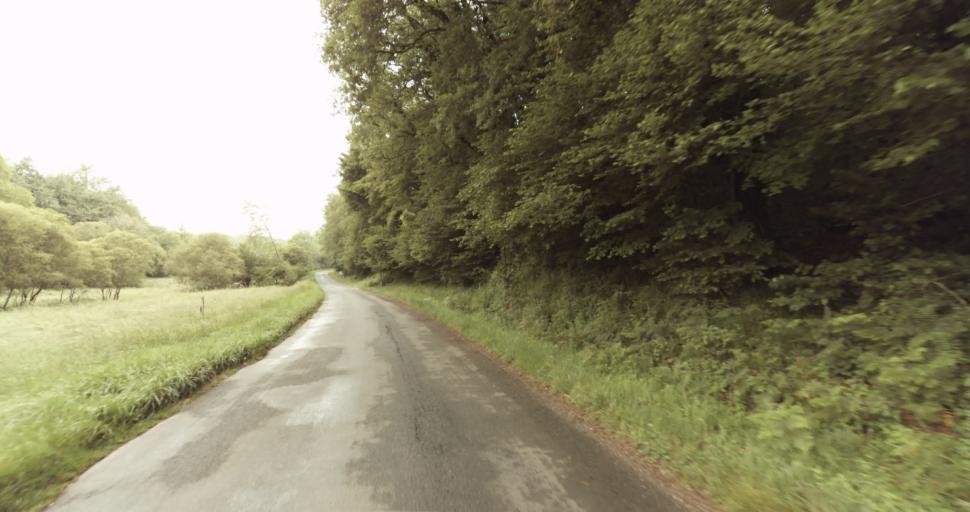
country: FR
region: Aquitaine
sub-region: Departement de la Dordogne
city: Lalinde
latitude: 44.8849
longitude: 0.7748
